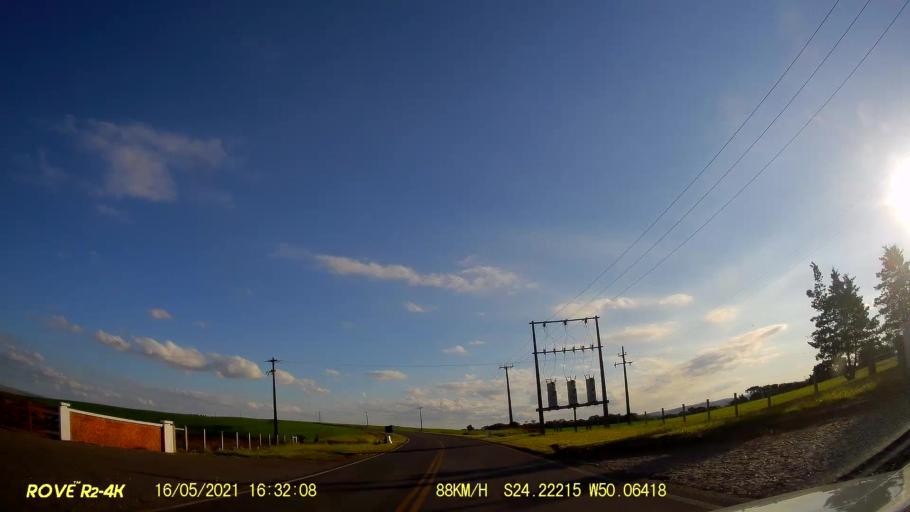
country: BR
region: Parana
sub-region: Pirai Do Sul
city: Pirai do Sul
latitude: -24.2228
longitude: -50.0640
